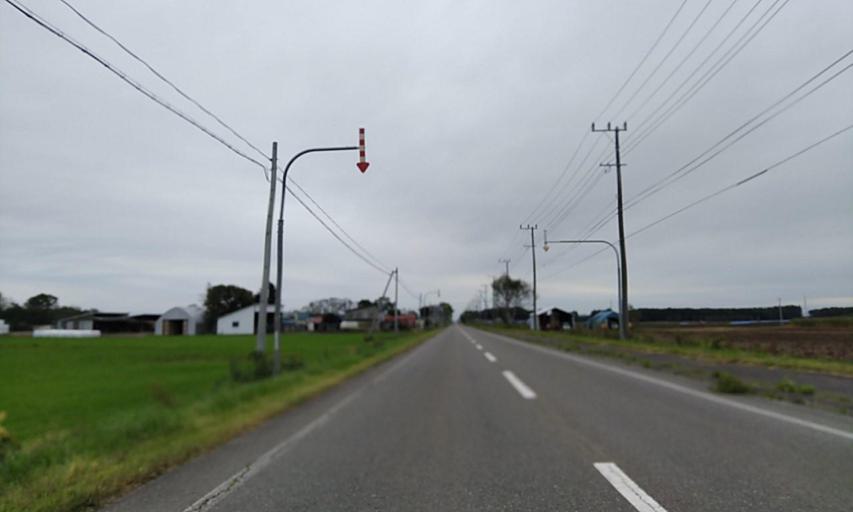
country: JP
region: Hokkaido
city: Obihiro
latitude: 42.6409
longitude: 143.0949
